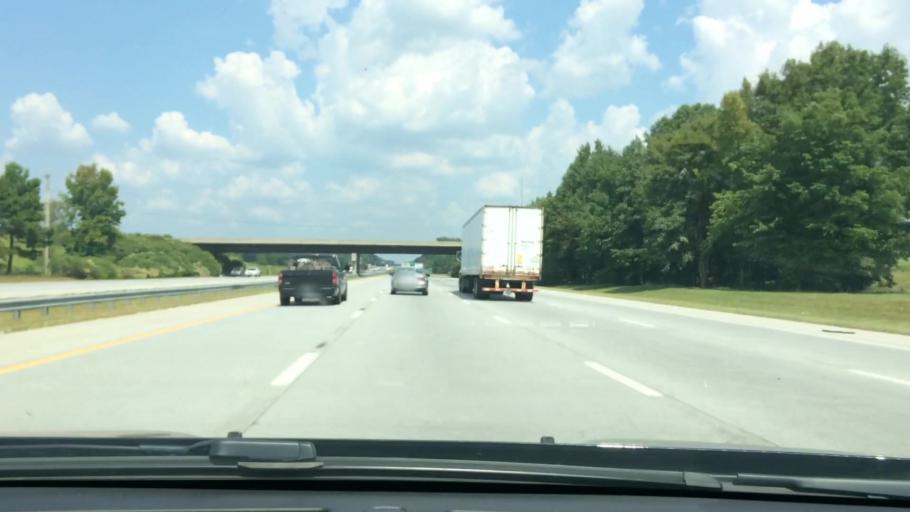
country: US
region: North Carolina
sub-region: Rowan County
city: China Grove
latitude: 35.5981
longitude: -80.5331
